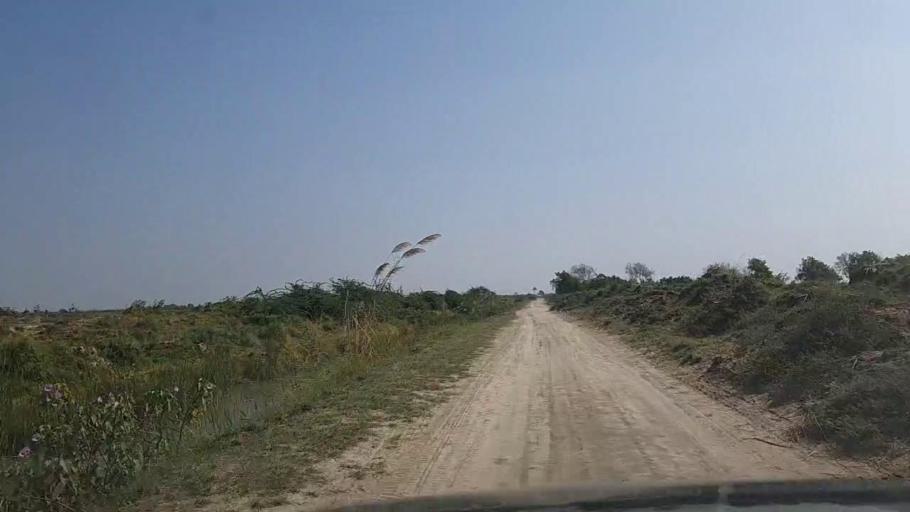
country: PK
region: Sindh
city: Gharo
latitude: 24.7155
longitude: 67.5717
